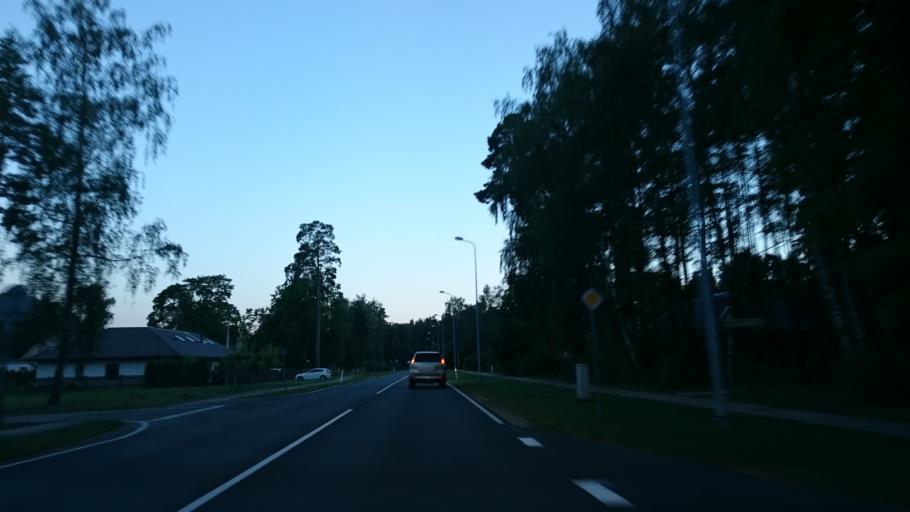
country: LV
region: Saulkrastu
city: Saulkrasti
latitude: 57.2383
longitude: 24.3969
